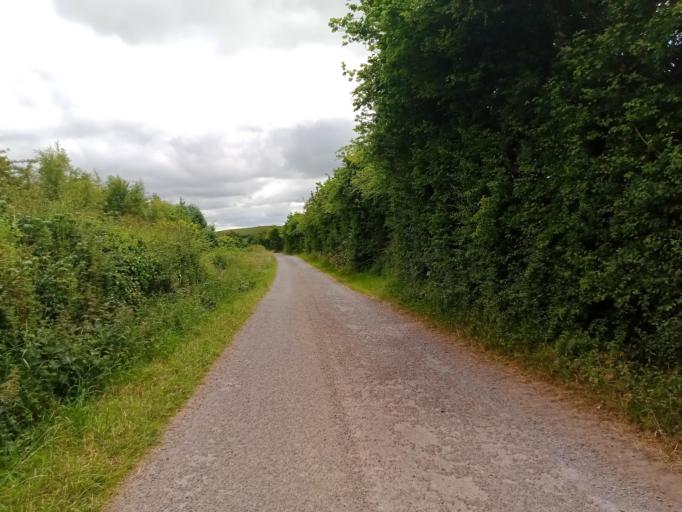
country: IE
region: Leinster
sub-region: Laois
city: Rathdowney
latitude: 52.7910
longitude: -7.4811
